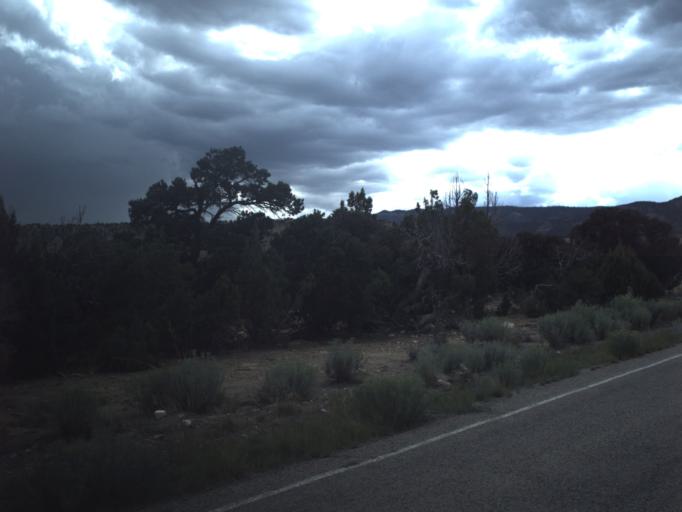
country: US
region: Utah
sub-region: Emery County
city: Huntington
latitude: 39.4863
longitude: -110.9519
